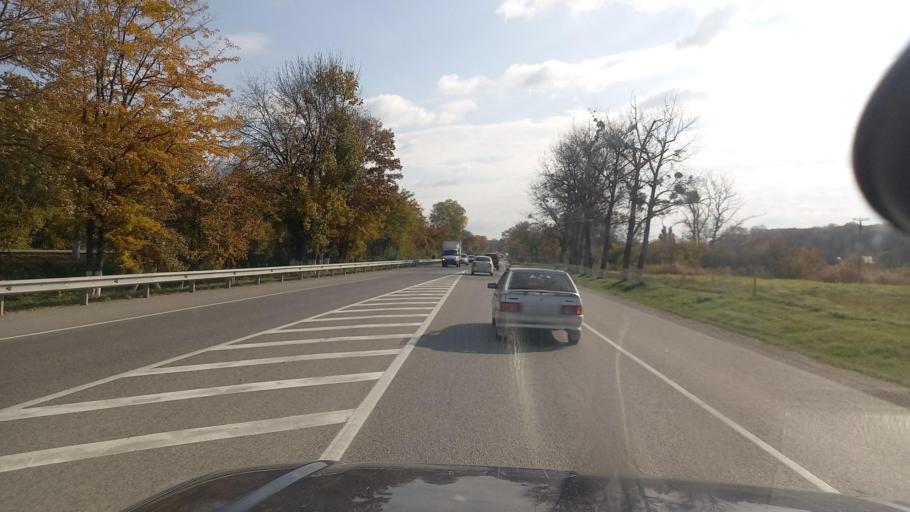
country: RU
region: Krasnodarskiy
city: Gayduk
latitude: 44.8723
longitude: 37.8340
